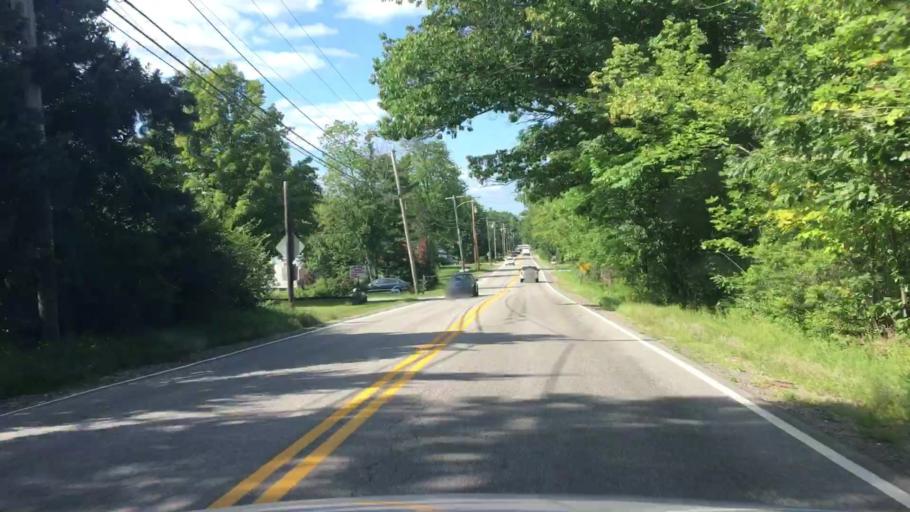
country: US
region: Maine
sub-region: Cumberland County
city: Westbrook
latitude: 43.7277
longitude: -70.3427
